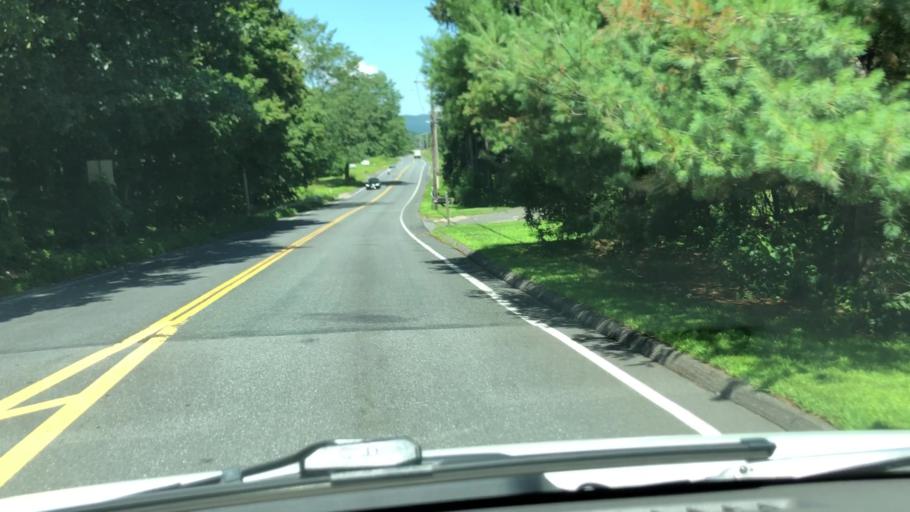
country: US
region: Massachusetts
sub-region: Hampshire County
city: Amherst Center
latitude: 42.3728
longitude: -72.5491
